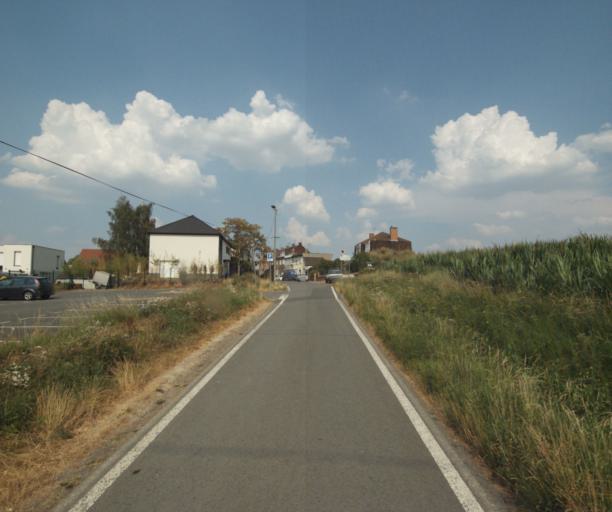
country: FR
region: Nord-Pas-de-Calais
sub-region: Departement du Nord
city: Linselles
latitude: 50.7326
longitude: 3.0730
